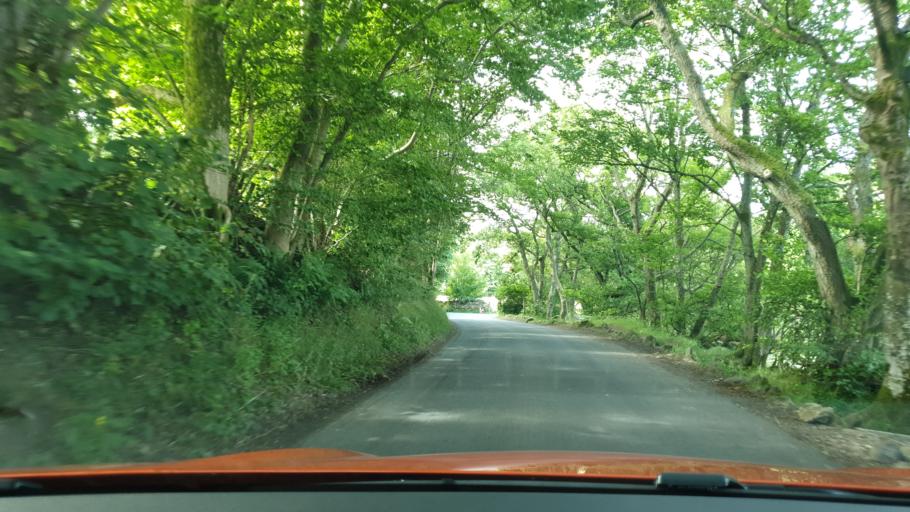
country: GB
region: England
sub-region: Cumbria
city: Penrith
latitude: 54.5713
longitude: -2.8611
